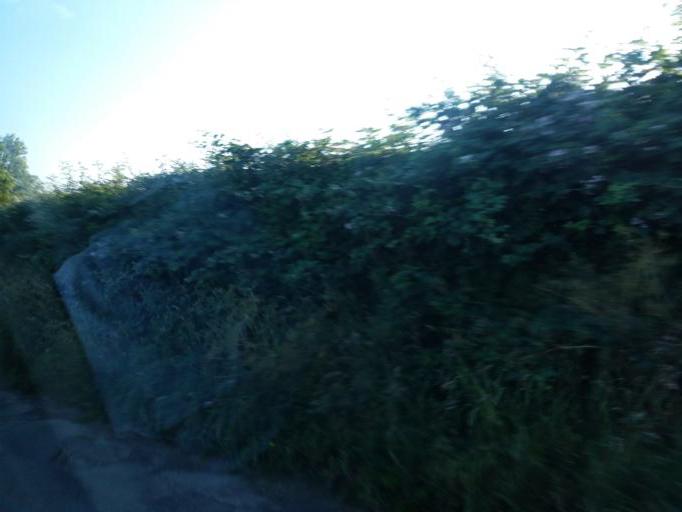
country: IE
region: Leinster
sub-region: An Mhi
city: Ashbourne
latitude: 53.5428
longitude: -6.3617
